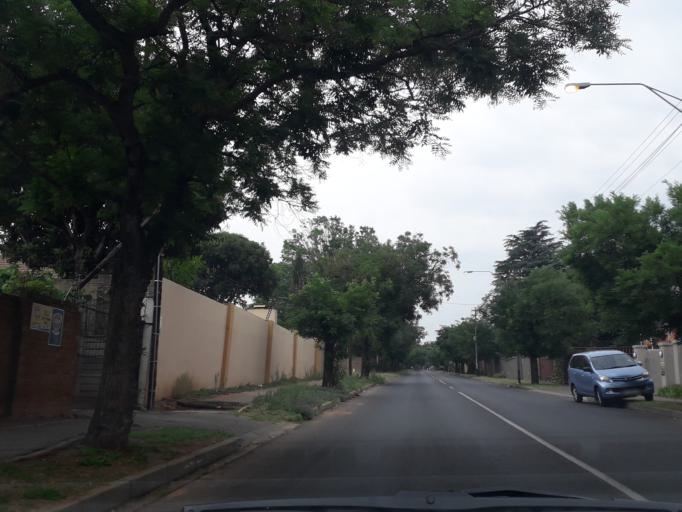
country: ZA
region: Gauteng
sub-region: City of Johannesburg Metropolitan Municipality
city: Johannesburg
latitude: -26.1418
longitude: 28.0944
